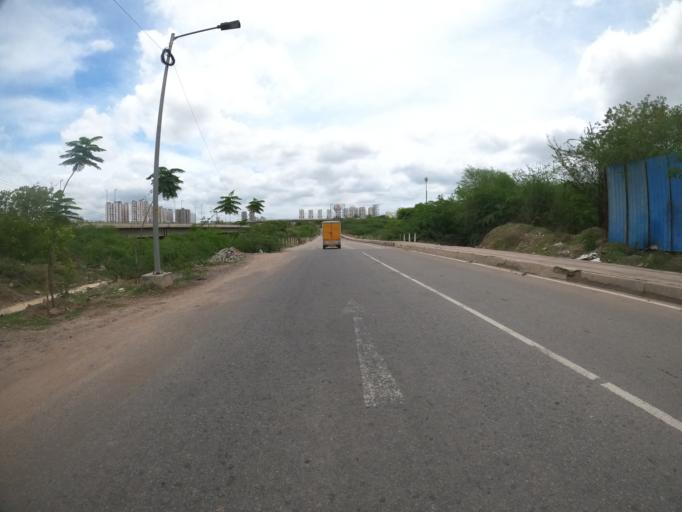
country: IN
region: Telangana
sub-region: Hyderabad
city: Hyderabad
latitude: 17.3826
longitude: 78.3510
